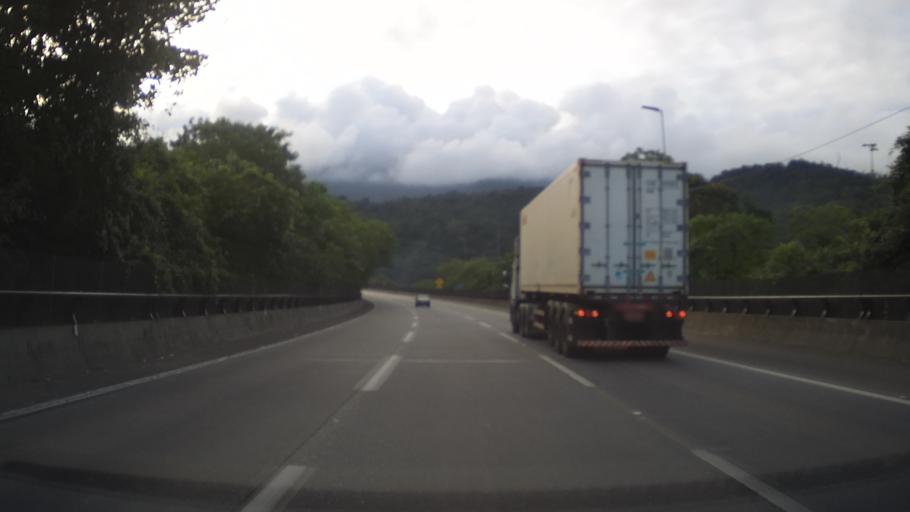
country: BR
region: Sao Paulo
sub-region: Cubatao
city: Cubatao
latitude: -23.9038
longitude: -46.4501
